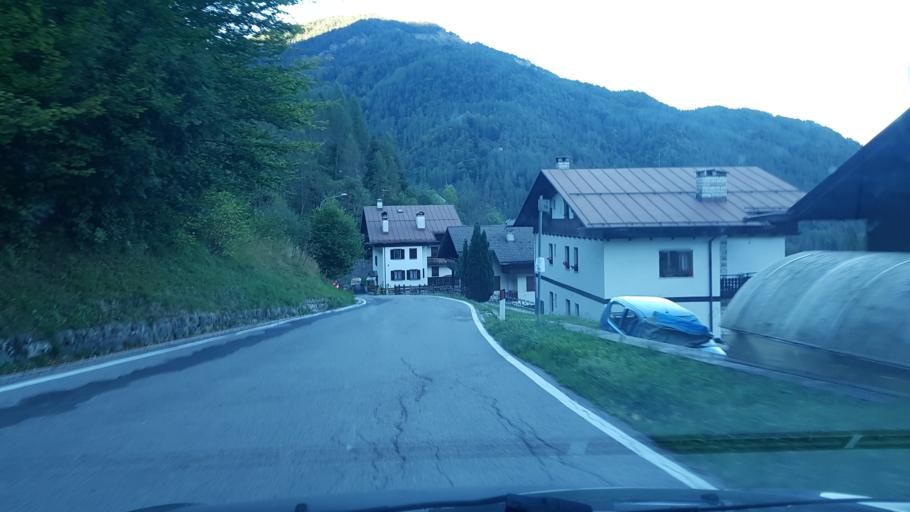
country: IT
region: Veneto
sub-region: Provincia di Belluno
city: Fusine
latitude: 46.3524
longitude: 12.1374
